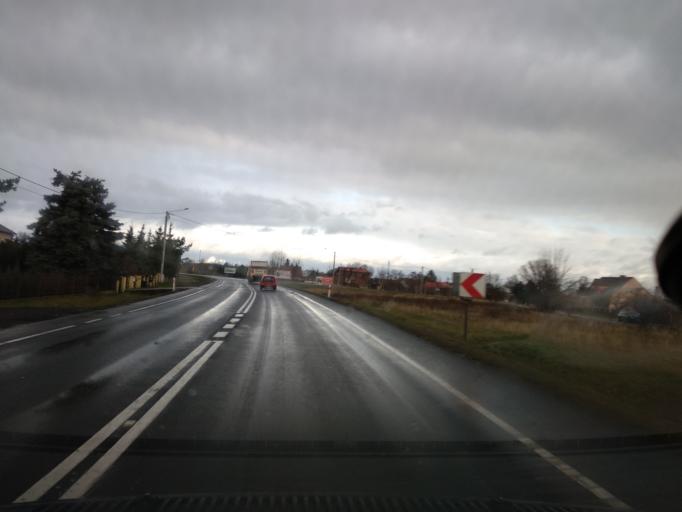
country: PL
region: Greater Poland Voivodeship
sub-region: Powiat koninski
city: Stare Miasto
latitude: 52.1531
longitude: 18.2051
